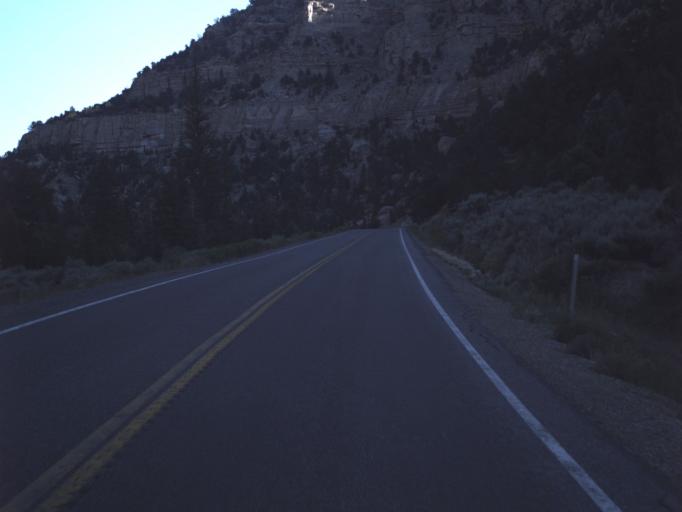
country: US
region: Utah
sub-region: Emery County
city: Huntington
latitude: 39.4200
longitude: -111.1246
